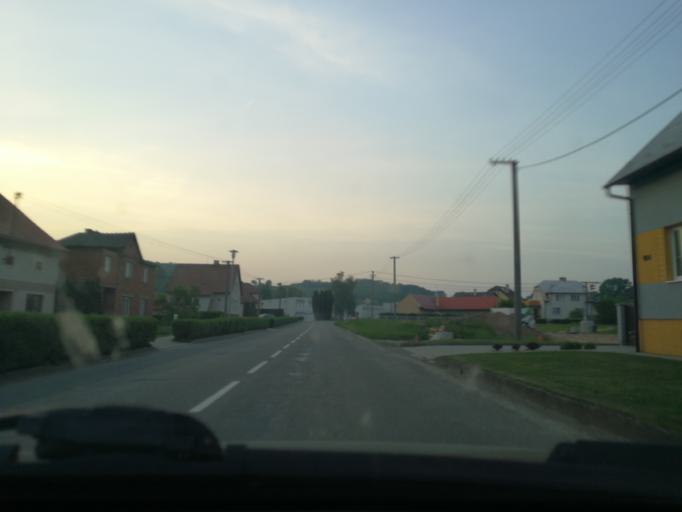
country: CZ
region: Zlin
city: Tecovice
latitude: 49.2442
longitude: 17.5680
